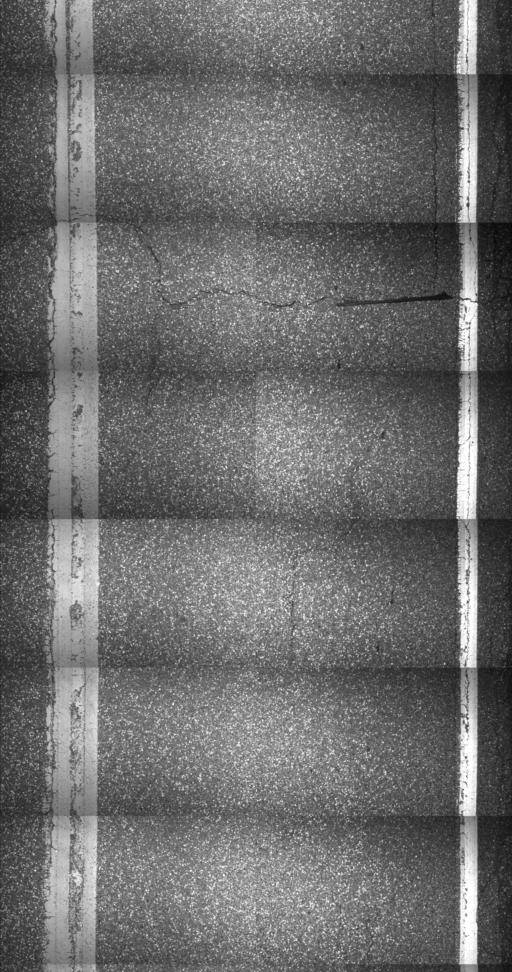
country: US
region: New Hampshire
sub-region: Grafton County
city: Lyme
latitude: 43.7858
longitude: -72.2055
